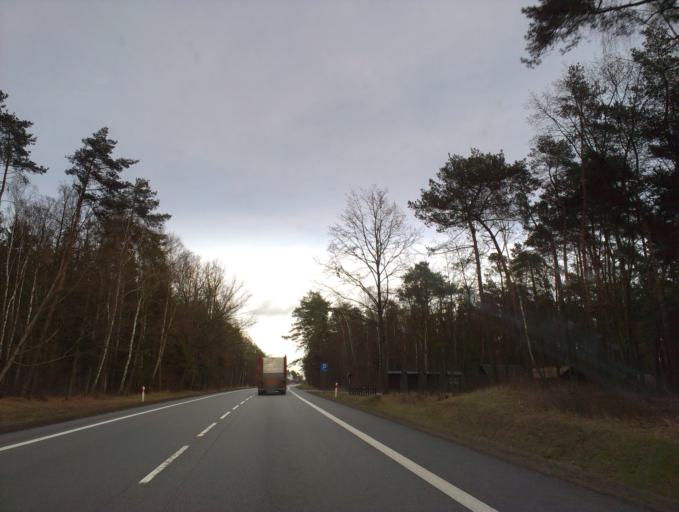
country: PL
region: Kujawsko-Pomorskie
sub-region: Powiat lipnowski
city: Skepe
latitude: 52.8836
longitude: 19.3885
